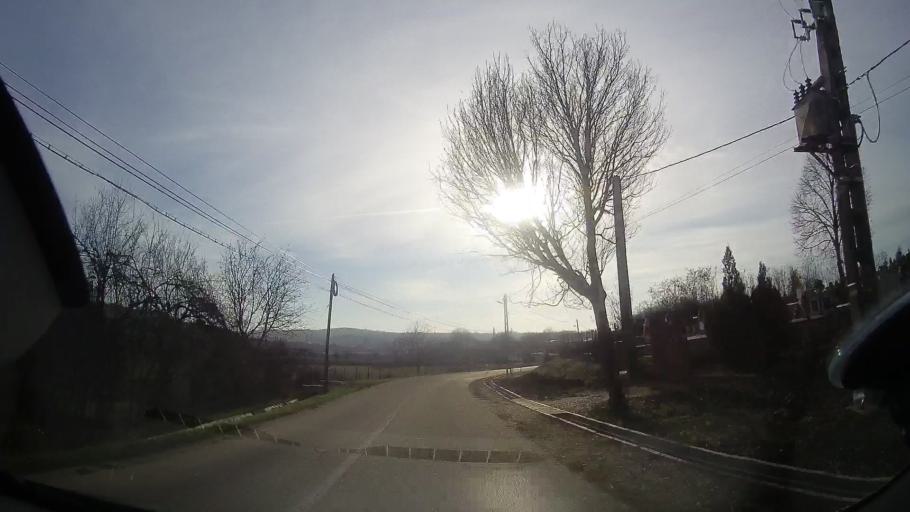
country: RO
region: Bihor
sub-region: Comuna Sarbi
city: Sarbi
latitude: 47.1982
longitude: 22.1250
